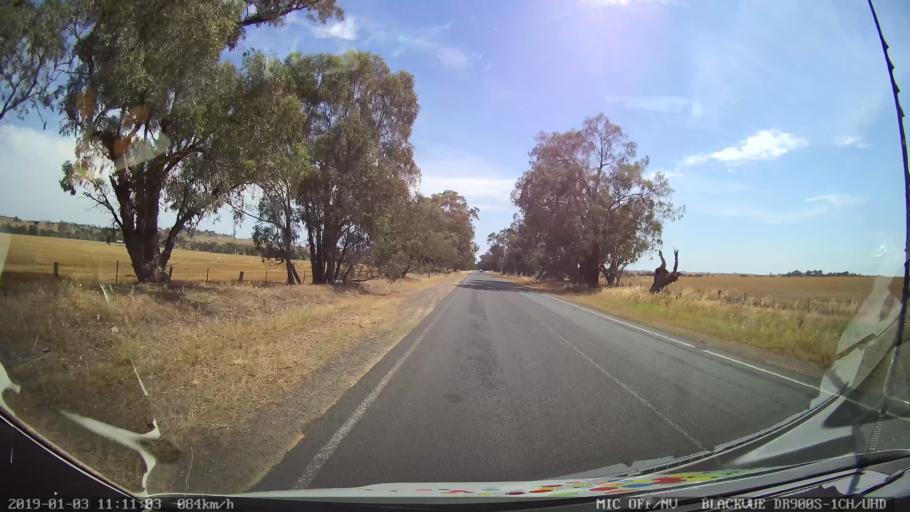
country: AU
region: New South Wales
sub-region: Young
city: Young
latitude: -34.2195
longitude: 148.2591
